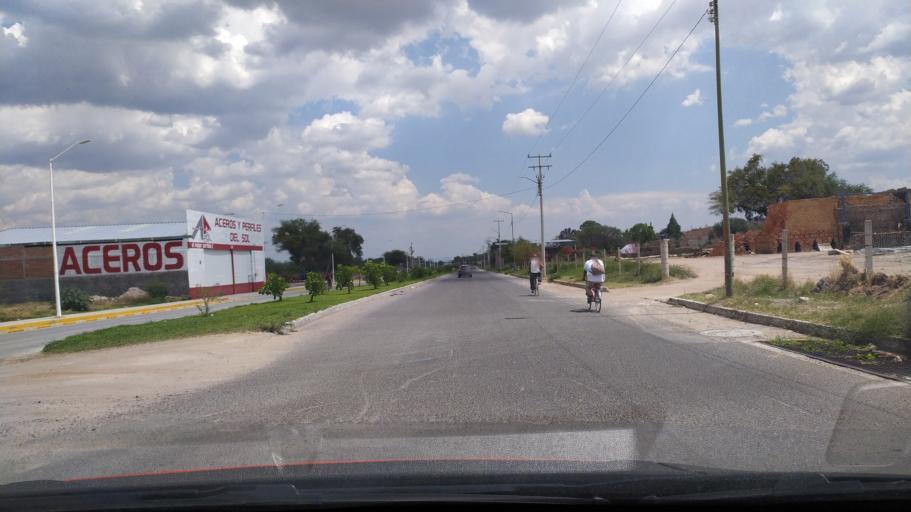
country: MX
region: Guanajuato
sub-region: Purisima del Rincon
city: Potrerillos (Guanajal)
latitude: 21.0499
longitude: -101.8691
